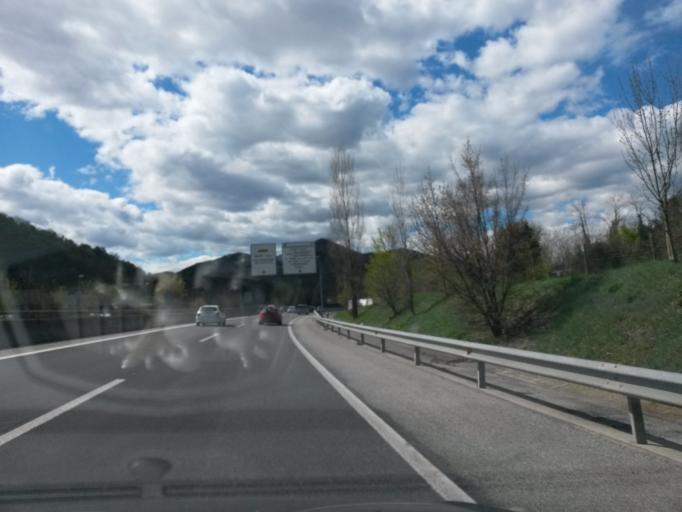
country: ES
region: Catalonia
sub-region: Provincia de Girona
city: MeteOlot
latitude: 42.1947
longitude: 2.5041
